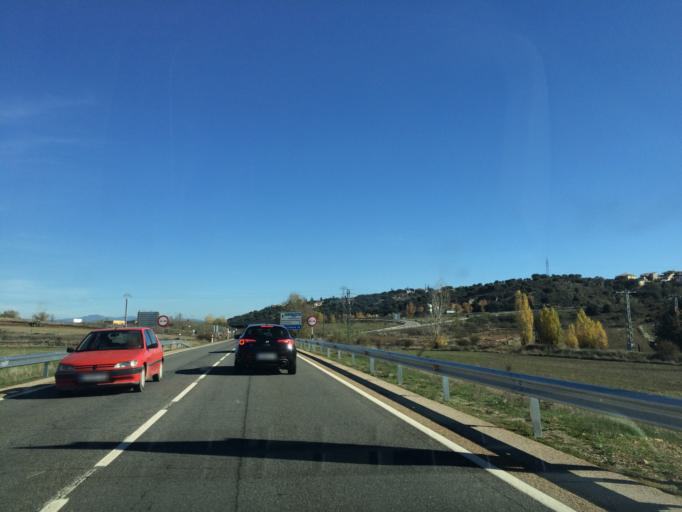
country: ES
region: Madrid
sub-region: Provincia de Madrid
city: Venturada
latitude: 40.7901
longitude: -3.6216
